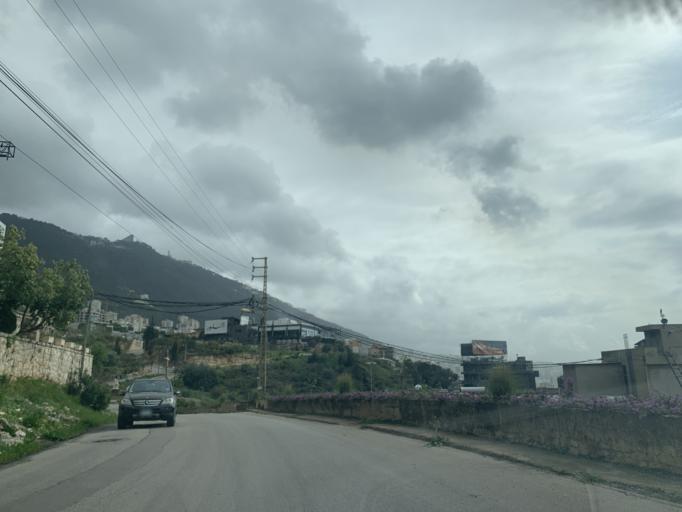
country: LB
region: Mont-Liban
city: Djounie
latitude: 34.0013
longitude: 35.6484
